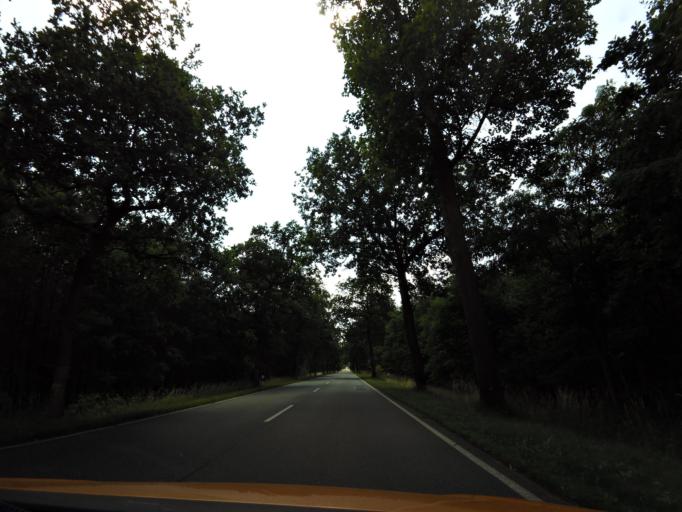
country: DE
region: Brandenburg
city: Dreetz
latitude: 52.8116
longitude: 12.5412
